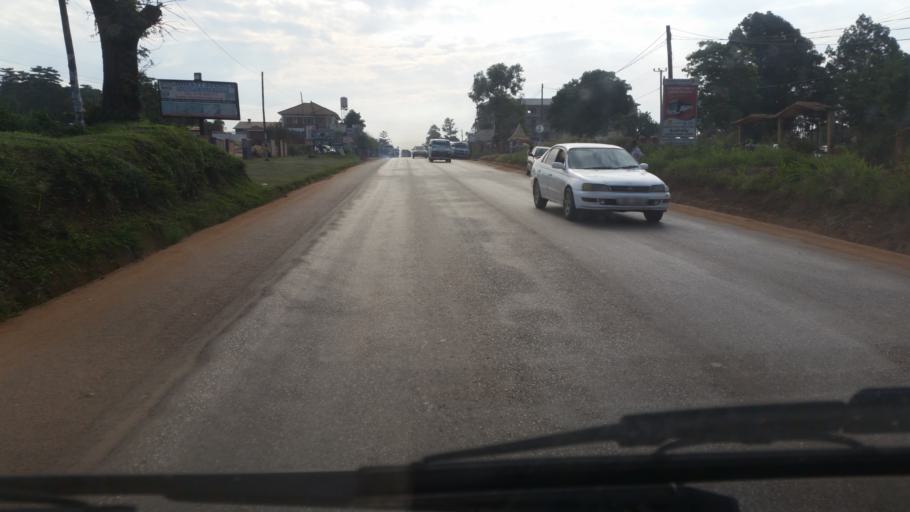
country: UG
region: Central Region
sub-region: Wakiso District
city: Bweyogerere
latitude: 0.3639
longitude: 32.6994
